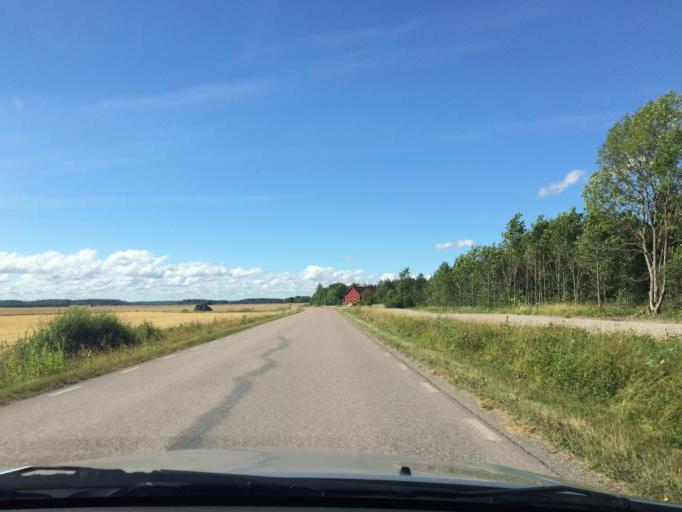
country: SE
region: Vaestmanland
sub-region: Vasteras
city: Vasteras
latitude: 59.5650
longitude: 16.4798
